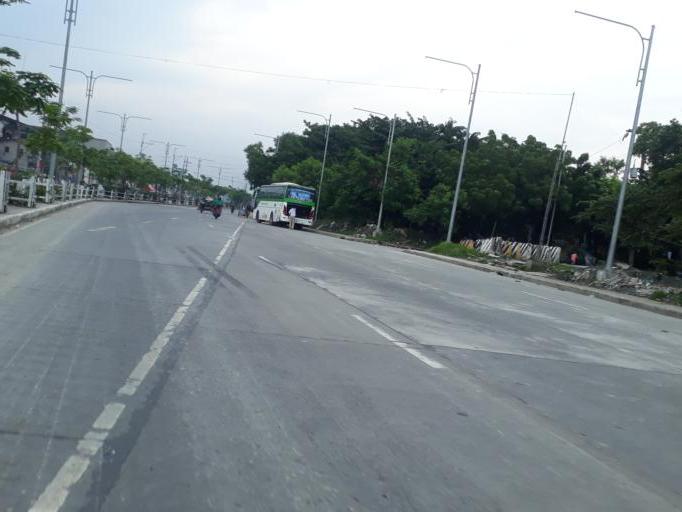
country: PH
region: Metro Manila
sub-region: Caloocan City
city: Niugan
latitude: 14.6486
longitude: 120.9495
